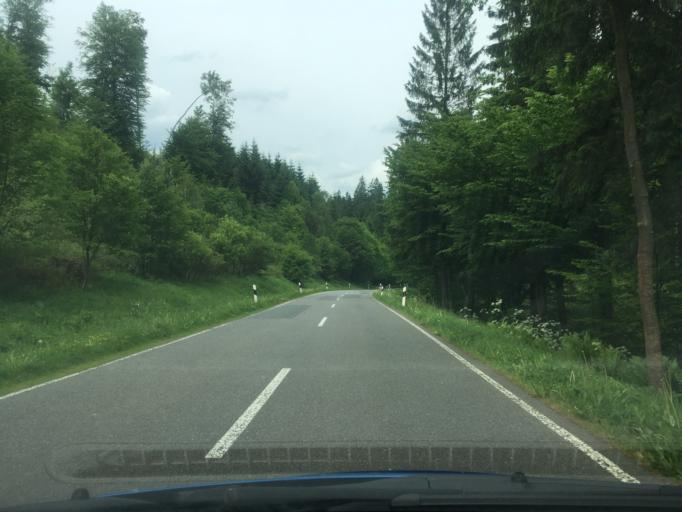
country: DE
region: Lower Saxony
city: Uslar
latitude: 51.7332
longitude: 9.6358
